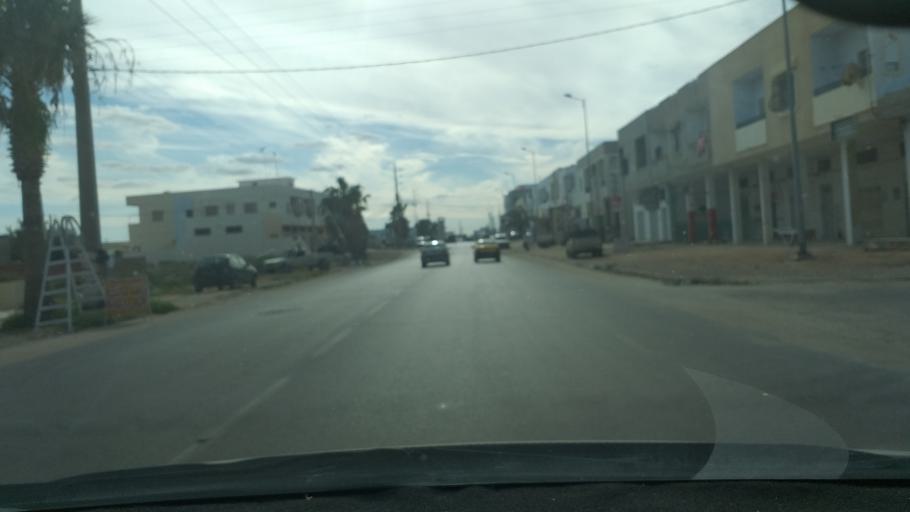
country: TN
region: Safaqis
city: Al Qarmadah
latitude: 34.7895
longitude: 10.8036
